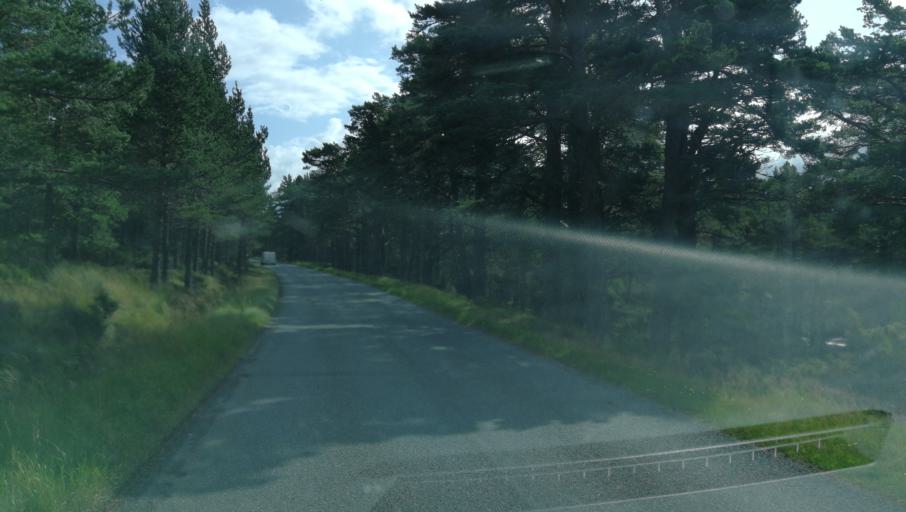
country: GB
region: Scotland
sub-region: Highland
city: Aviemore
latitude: 57.1716
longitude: -3.7468
